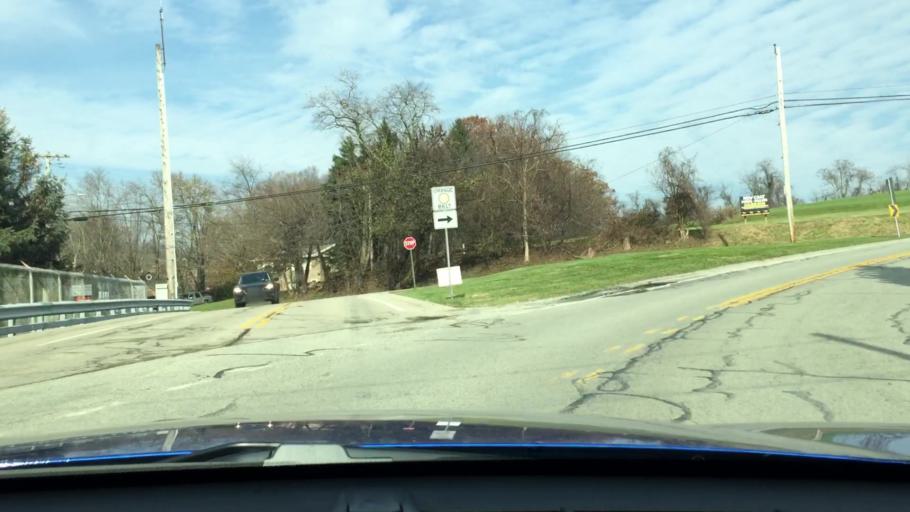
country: US
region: Pennsylvania
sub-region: Allegheny County
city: Elizabeth
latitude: 40.2551
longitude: -79.8531
